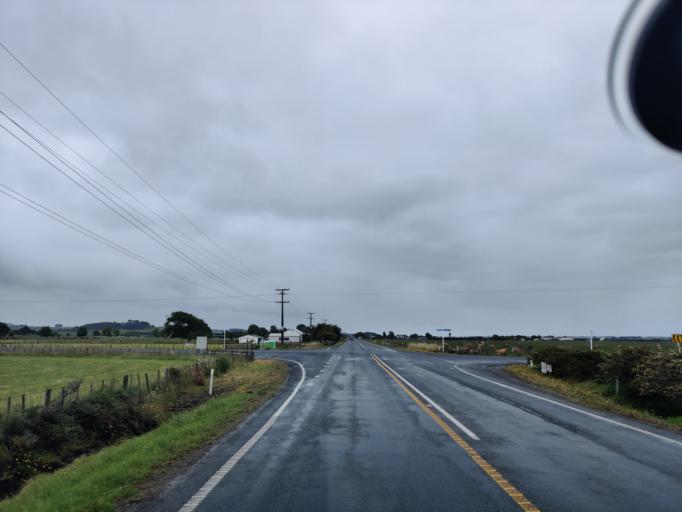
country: NZ
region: Northland
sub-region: Kaipara District
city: Dargaville
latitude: -35.9515
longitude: 173.8923
